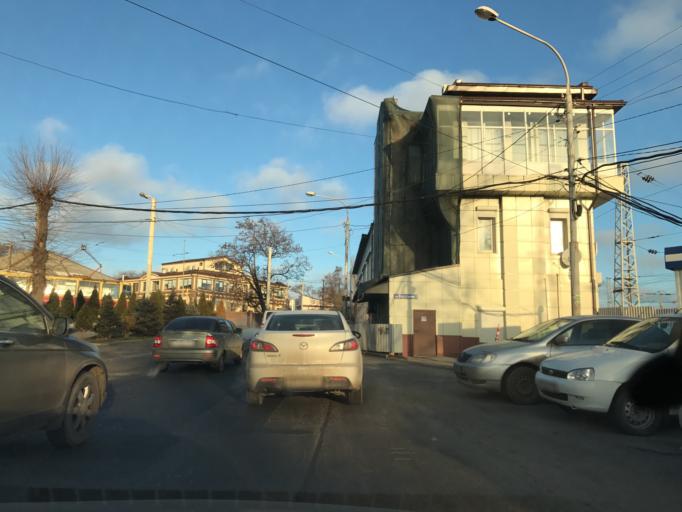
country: RU
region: Rostov
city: Rostov-na-Donu
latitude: 47.2204
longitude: 39.6863
